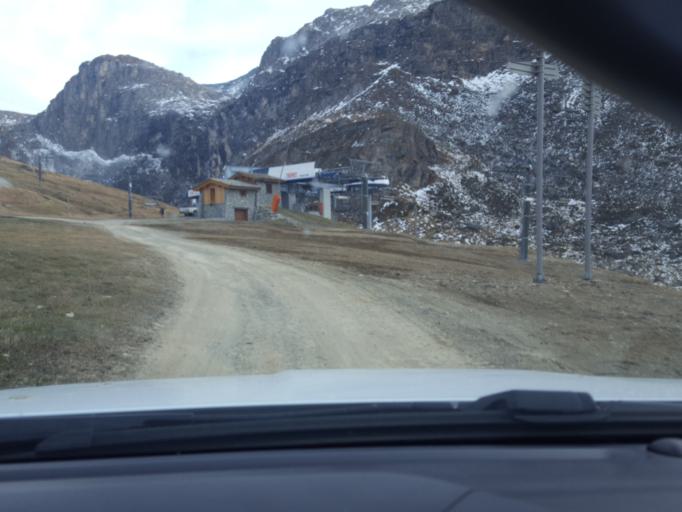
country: FR
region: Rhone-Alpes
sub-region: Departement de la Savoie
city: Tignes
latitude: 45.4522
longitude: 6.9047
